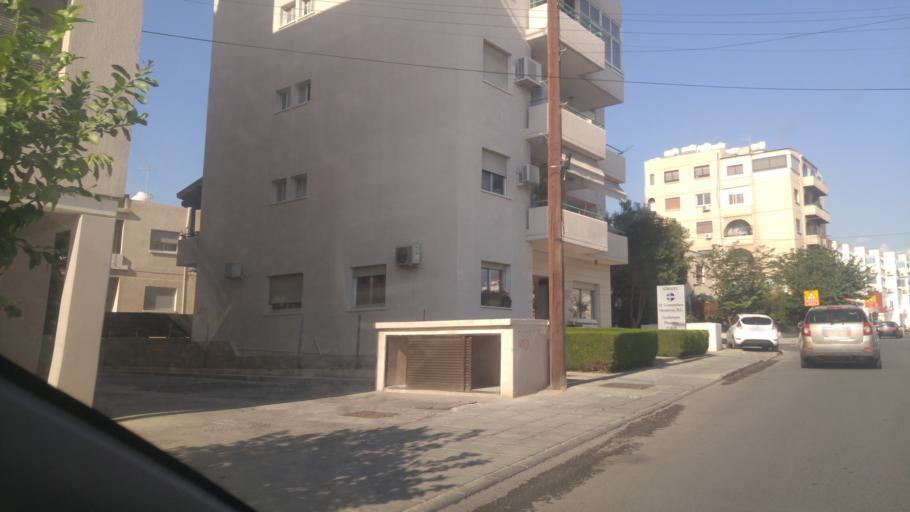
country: CY
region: Limassol
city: Limassol
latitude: 34.6933
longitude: 33.0519
